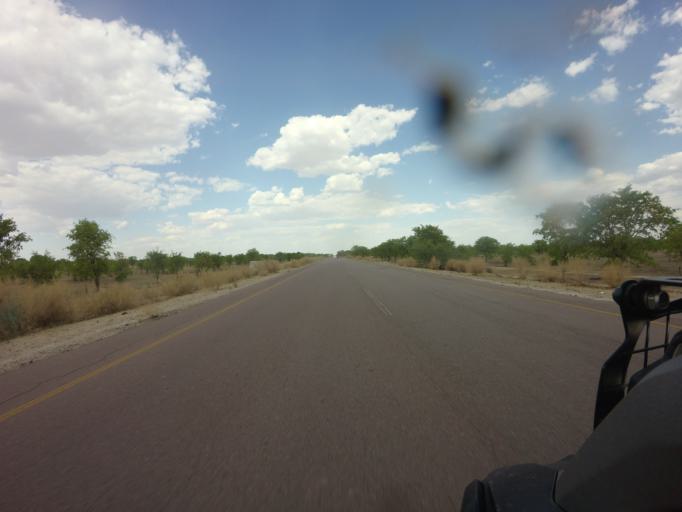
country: AO
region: Cunene
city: Ondjiva
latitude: -16.7378
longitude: 15.1359
